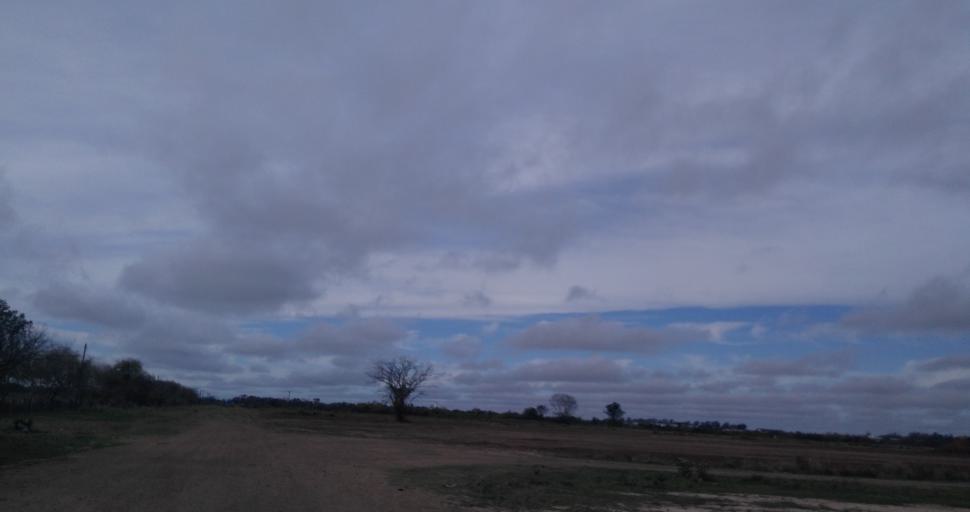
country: AR
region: Chaco
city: Fontana
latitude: -27.3902
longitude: -58.9834
